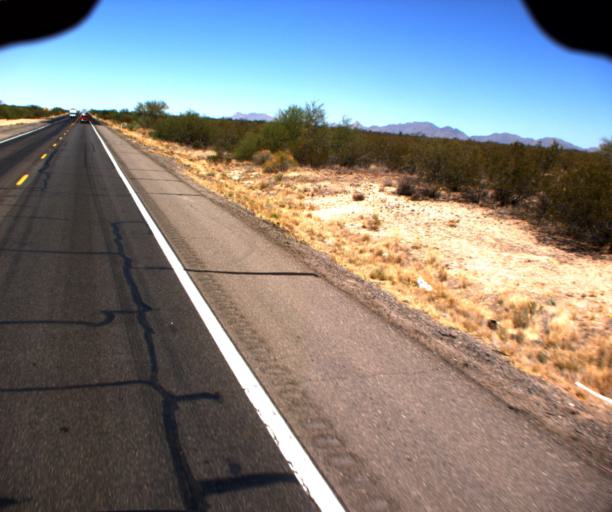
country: US
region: Arizona
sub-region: Yavapai County
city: Congress
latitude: 34.0513
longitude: -112.8470
